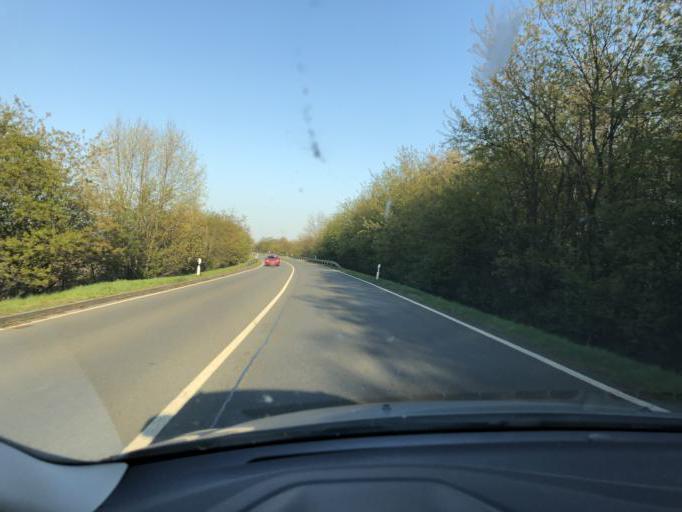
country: DE
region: Brandenburg
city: Ruhland
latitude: 51.4644
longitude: 13.8735
